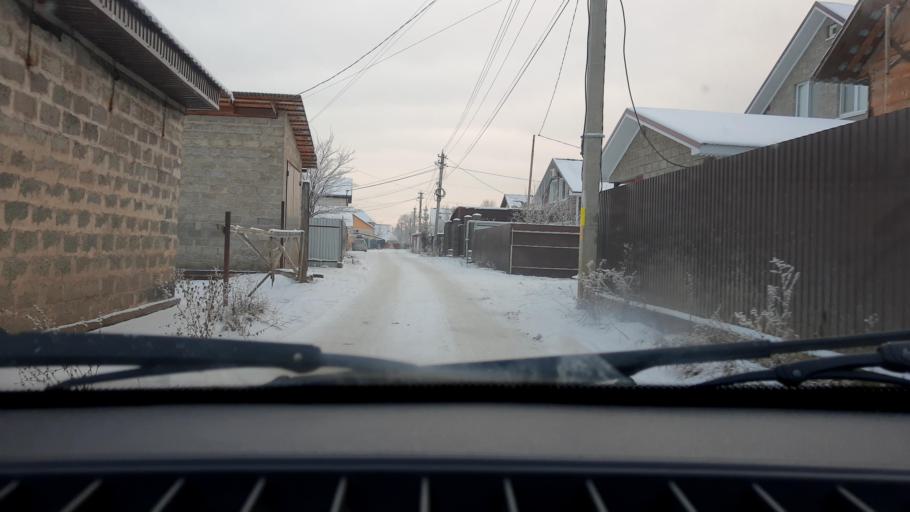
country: RU
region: Bashkortostan
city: Ufa
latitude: 54.6594
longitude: 55.9248
